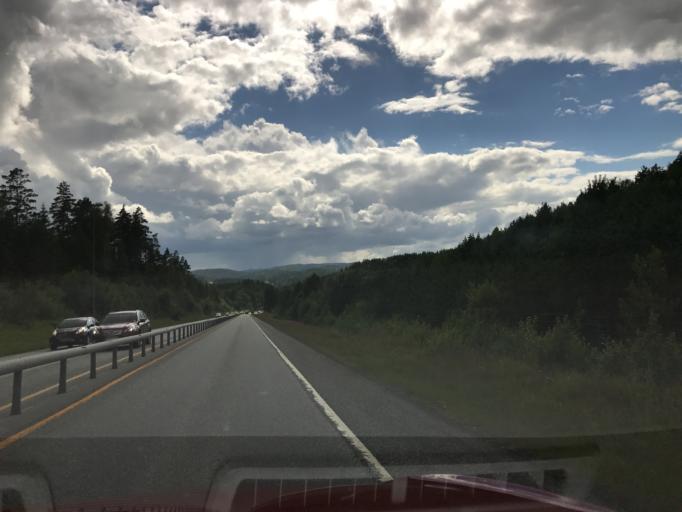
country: NO
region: Aust-Agder
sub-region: Gjerstad
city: Gjerstad
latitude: 58.8550
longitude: 9.1281
